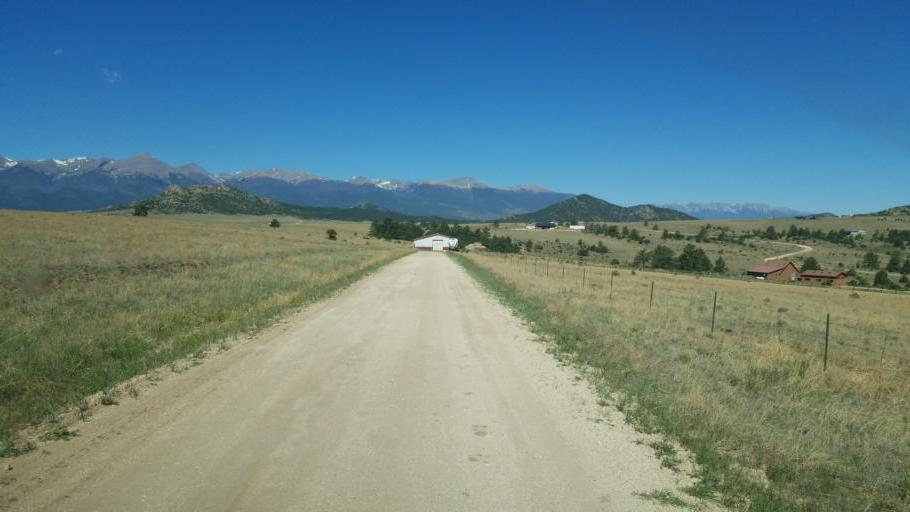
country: US
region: Colorado
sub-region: Custer County
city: Westcliffe
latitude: 38.2341
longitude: -105.4736
